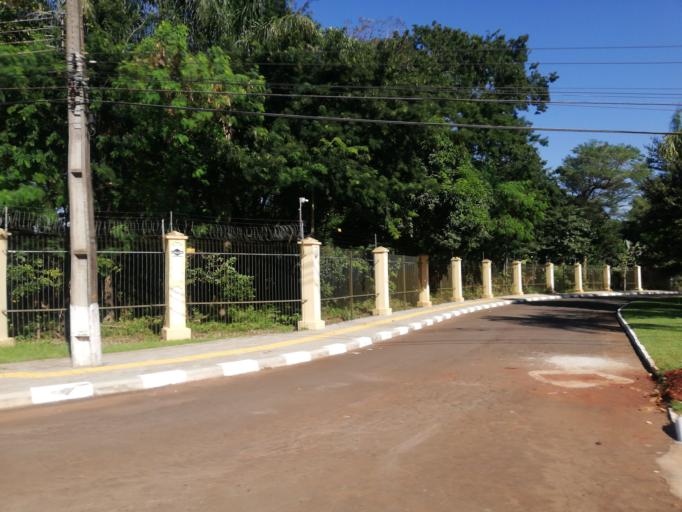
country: BR
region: Parana
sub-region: Foz Do Iguacu
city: Foz do Iguacu
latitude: -25.5591
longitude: -54.5629
